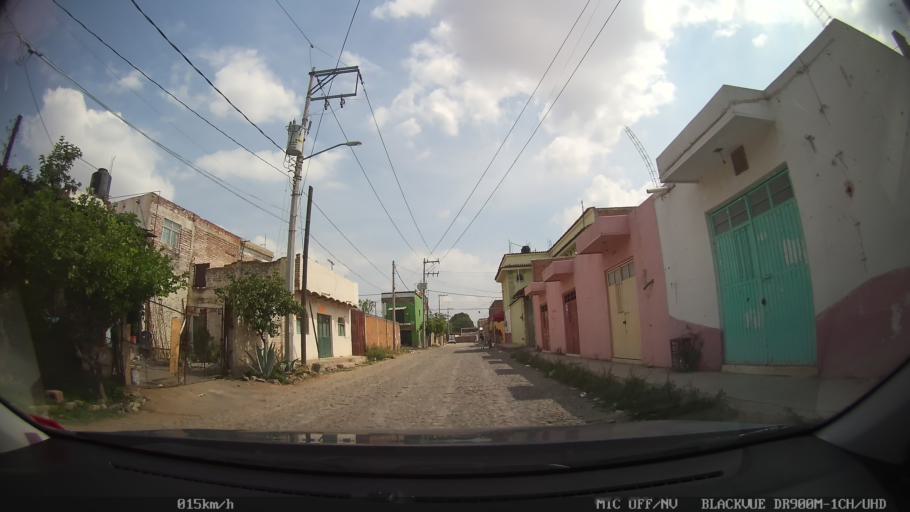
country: MX
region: Jalisco
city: Tonala
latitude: 20.6327
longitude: -103.2304
